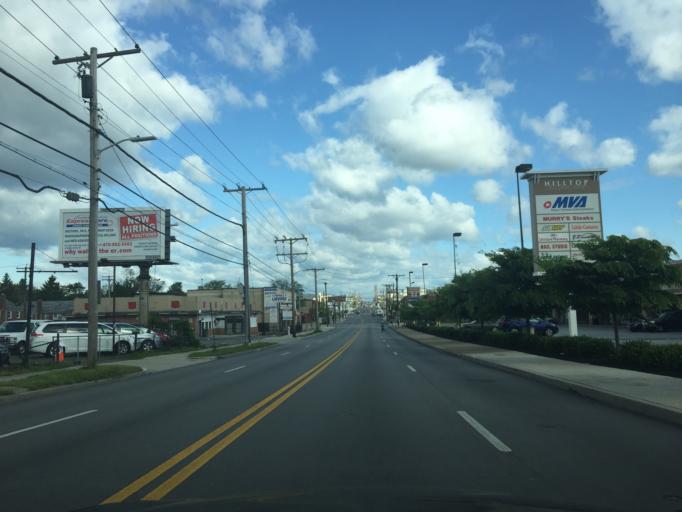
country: US
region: Maryland
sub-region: Baltimore County
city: Lochearn
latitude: 39.3466
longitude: -76.6888
